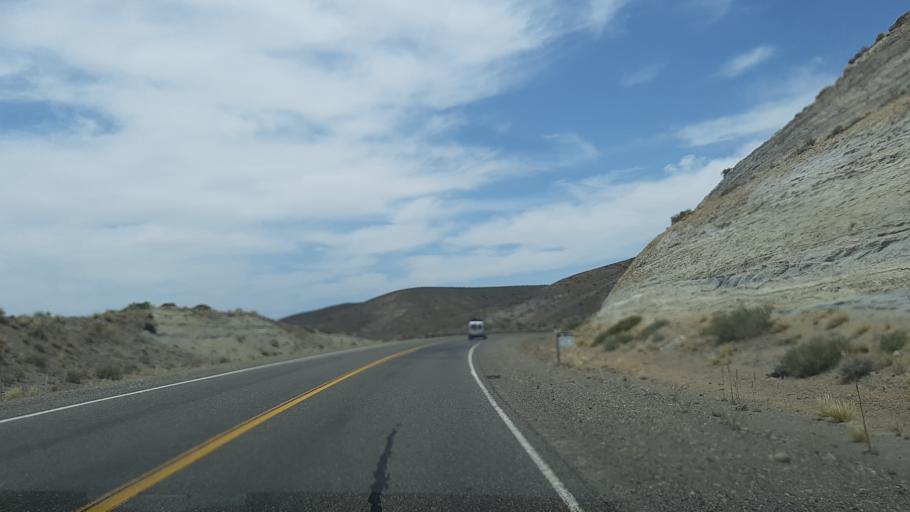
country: AR
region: Neuquen
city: Junin de los Andes
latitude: -40.4610
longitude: -70.6600
